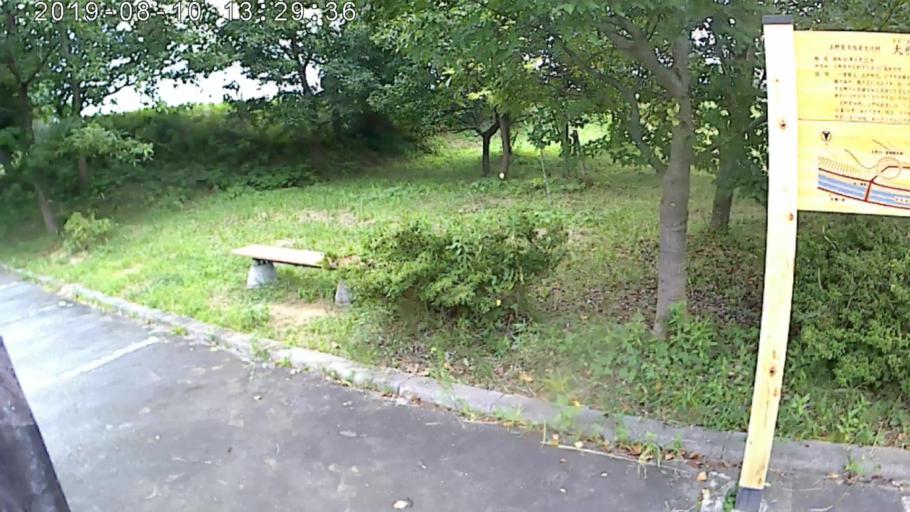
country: JP
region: Yamanashi
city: Uenohara
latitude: 35.6323
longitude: 139.0911
